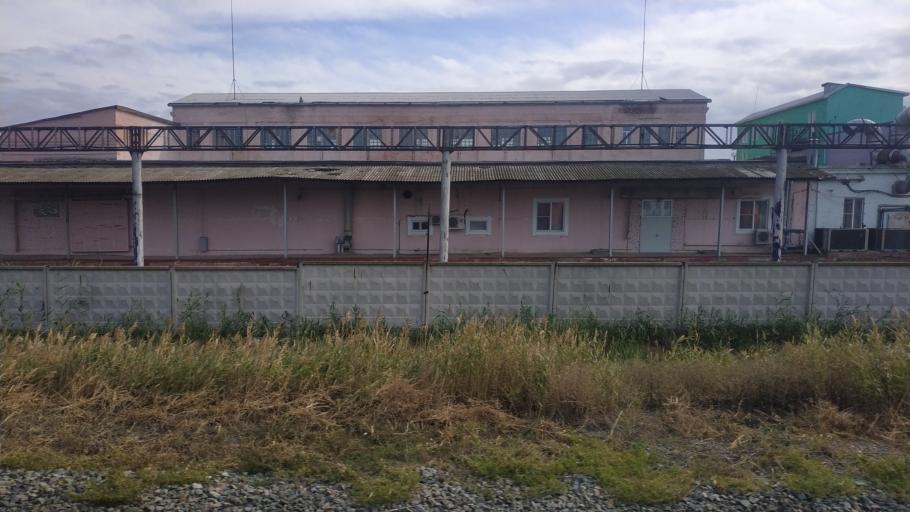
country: RU
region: Volgograd
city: Volgograd
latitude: 48.6021
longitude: 44.4344
